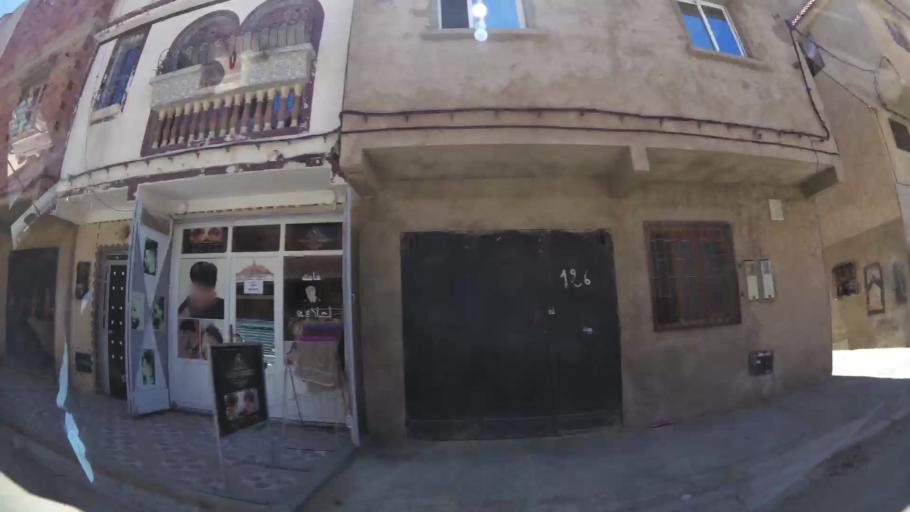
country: MA
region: Oriental
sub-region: Oujda-Angad
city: Oujda
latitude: 34.6610
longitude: -1.9276
